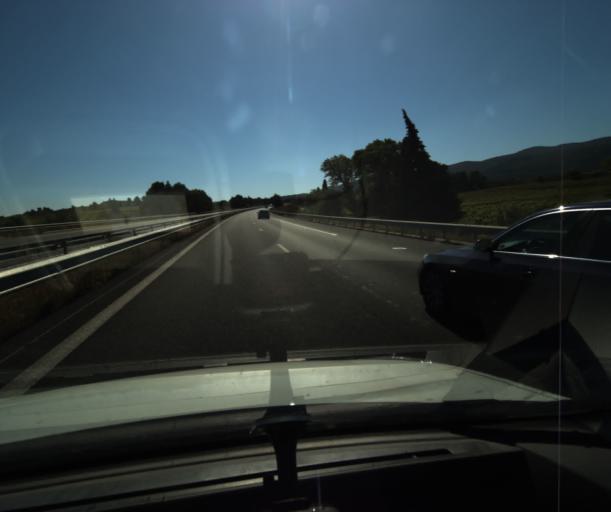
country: FR
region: Languedoc-Roussillon
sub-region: Departement de l'Aude
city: Capendu
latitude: 43.1792
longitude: 2.5843
